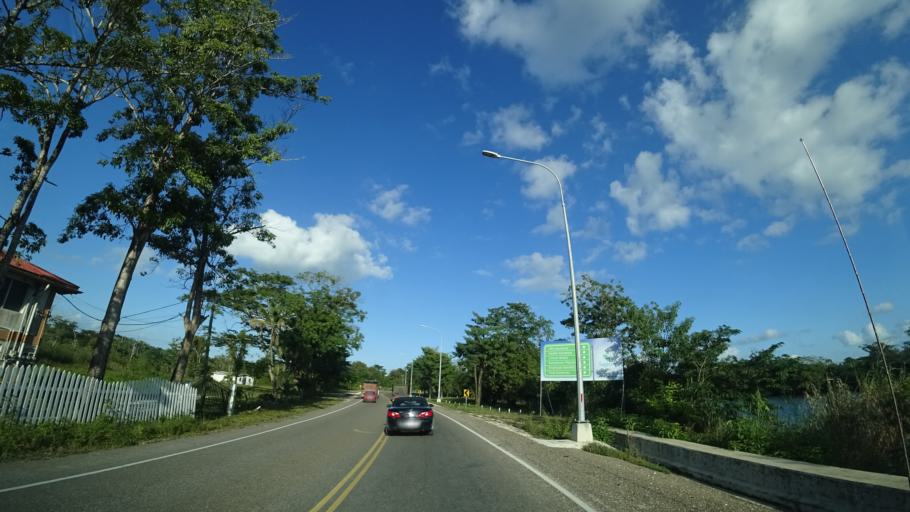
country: BZ
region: Belize
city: Belize City
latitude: 17.5455
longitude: -88.2808
